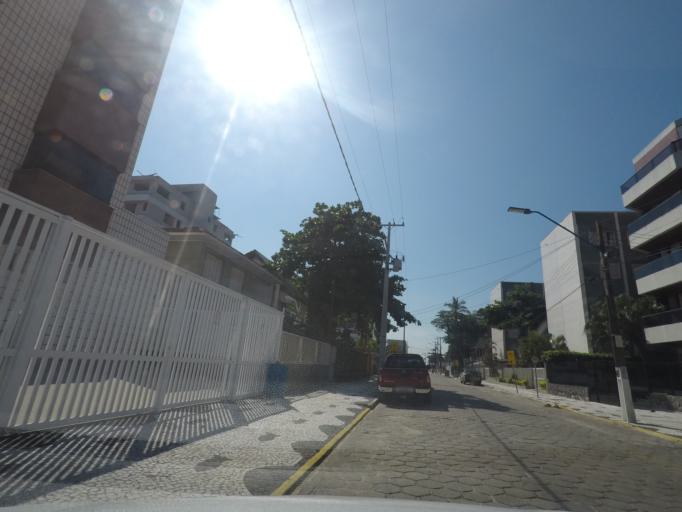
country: BR
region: Parana
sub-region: Guaratuba
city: Guaratuba
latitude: -25.8470
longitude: -48.5394
